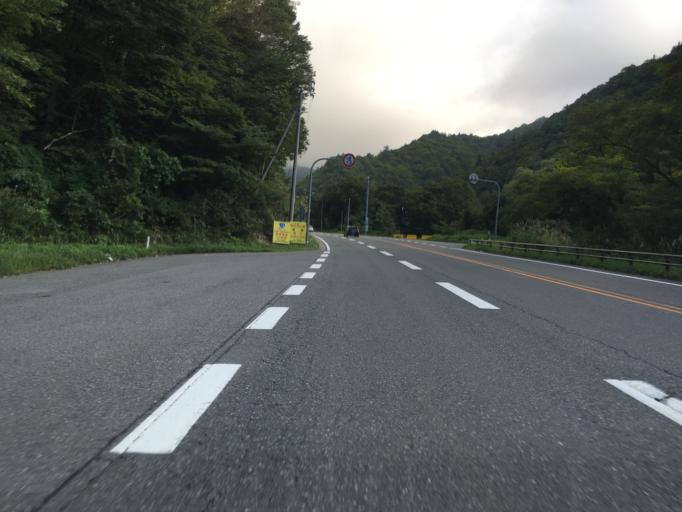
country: JP
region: Yamagata
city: Yonezawa
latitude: 37.8545
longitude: 140.2390
